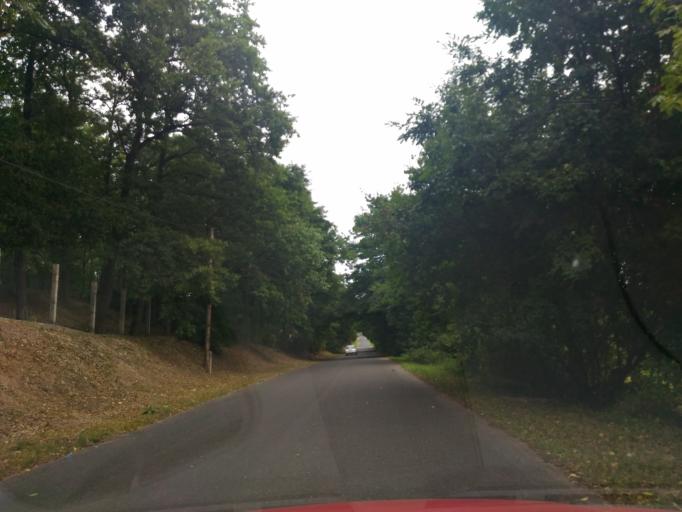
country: HU
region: Veszprem
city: Zanka
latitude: 46.8682
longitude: 17.6757
